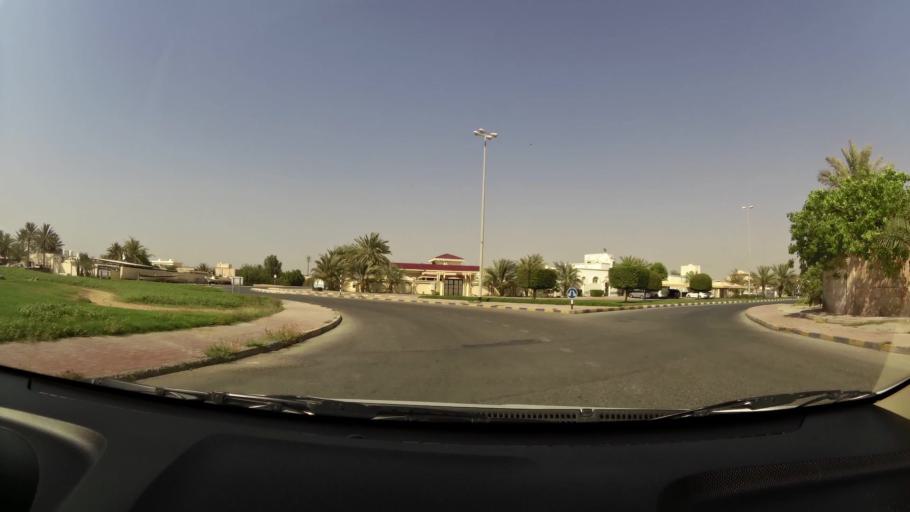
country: AE
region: Ajman
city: Ajman
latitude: 25.4146
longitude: 55.4726
